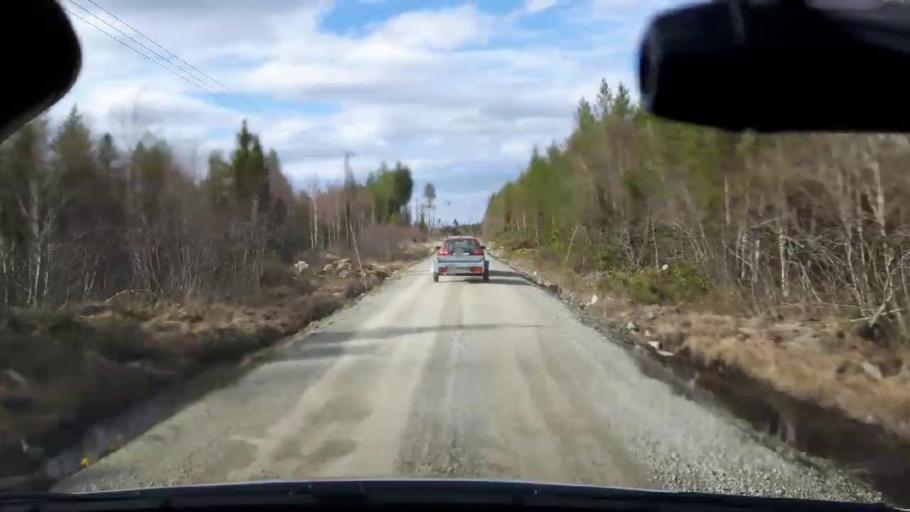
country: SE
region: Jaemtland
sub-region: Bergs Kommun
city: Hoverberg
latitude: 62.8434
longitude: 14.6674
